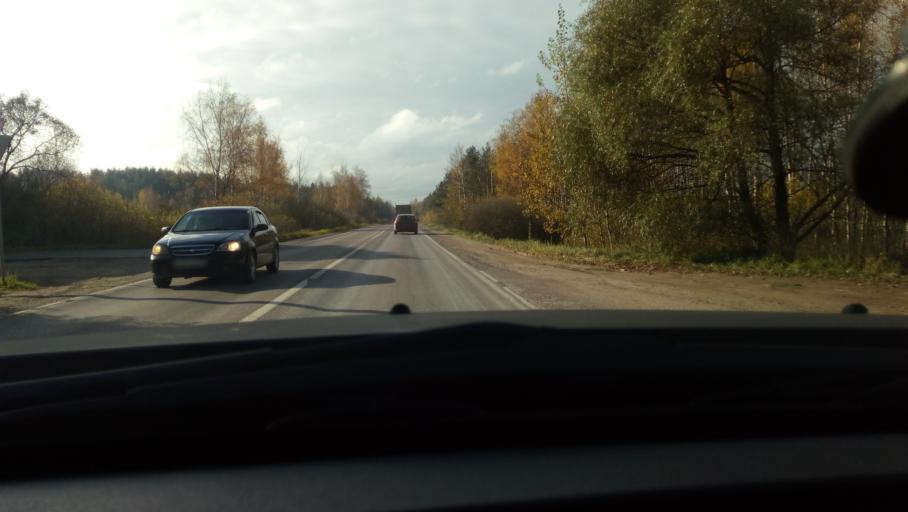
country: RU
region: Moskovskaya
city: Fryazevo
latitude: 55.7091
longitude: 38.4537
